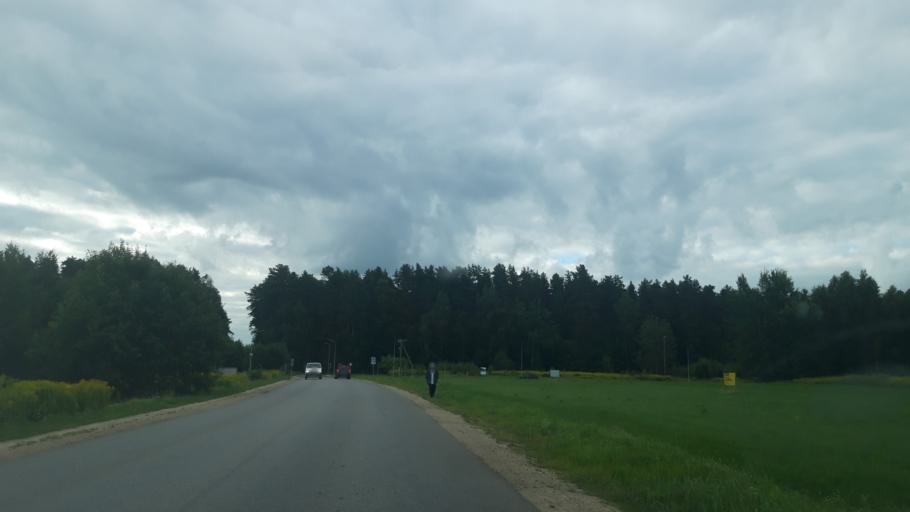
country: LV
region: Koceni
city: Koceni
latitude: 57.5223
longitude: 25.3816
